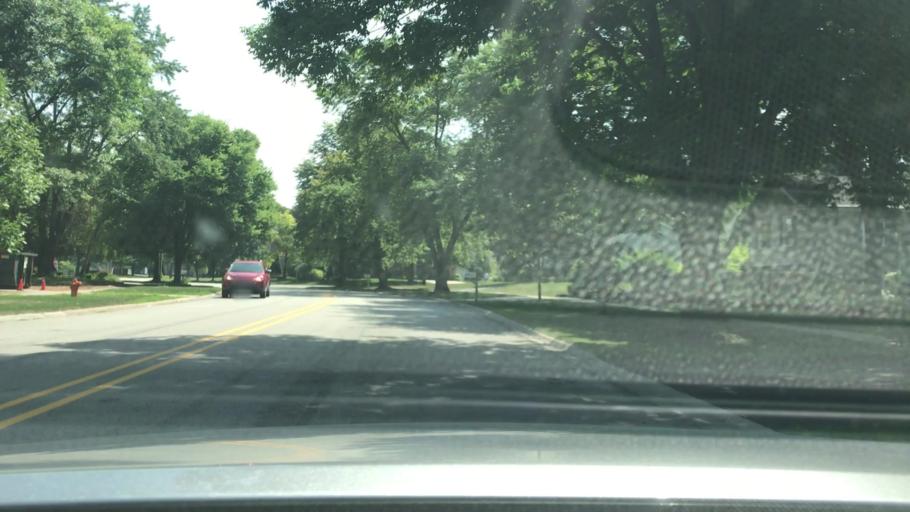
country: US
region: Illinois
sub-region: DuPage County
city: Naperville
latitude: 41.7411
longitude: -88.1119
